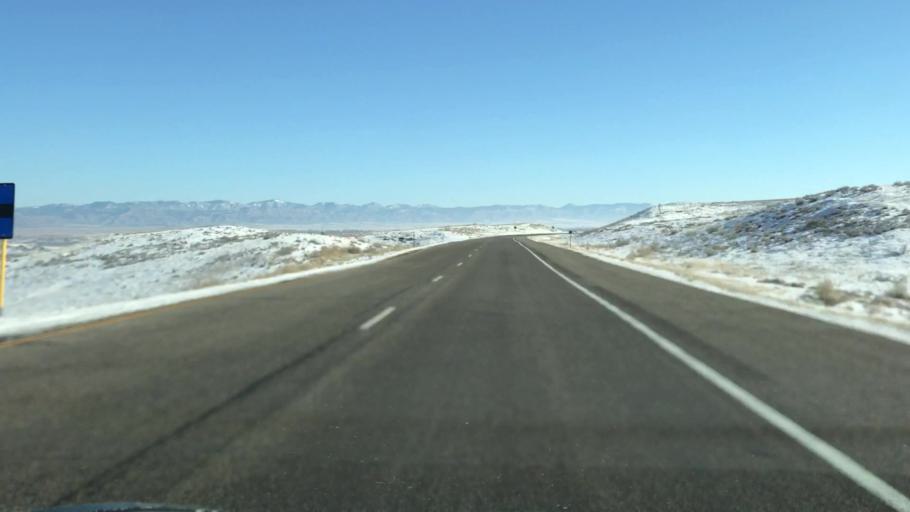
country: US
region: Colorado
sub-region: Mesa County
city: Loma
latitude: 39.2286
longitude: -108.9169
